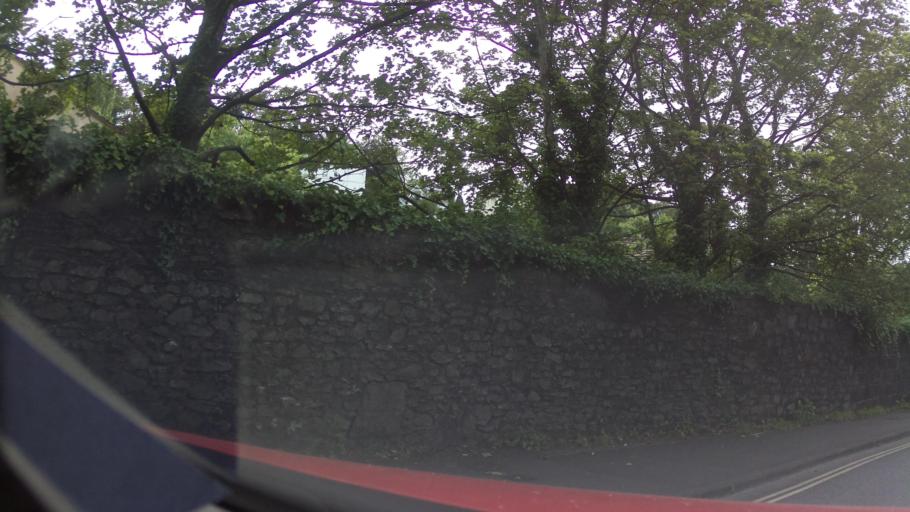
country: GB
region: England
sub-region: Borough of Torbay
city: Torquay
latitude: 50.4633
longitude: -3.5151
